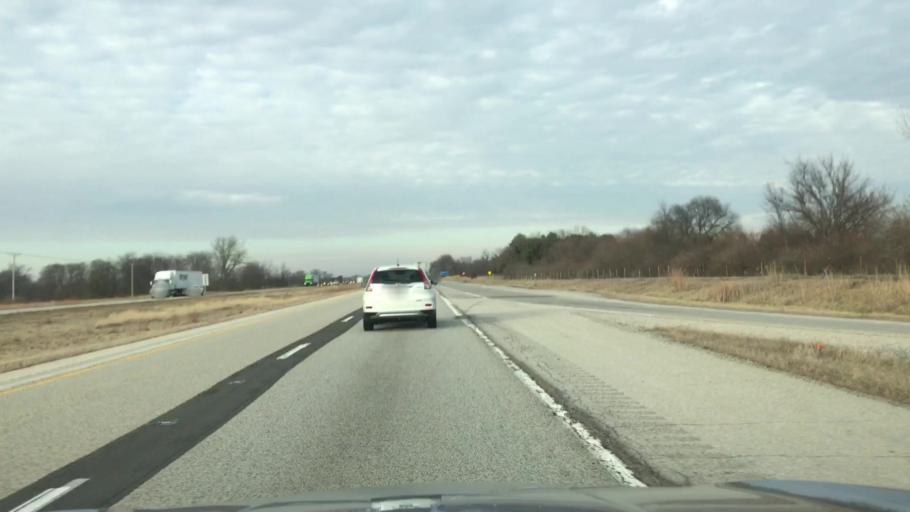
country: US
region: Illinois
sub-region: Sangamon County
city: Divernon
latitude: 39.5713
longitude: -89.6461
